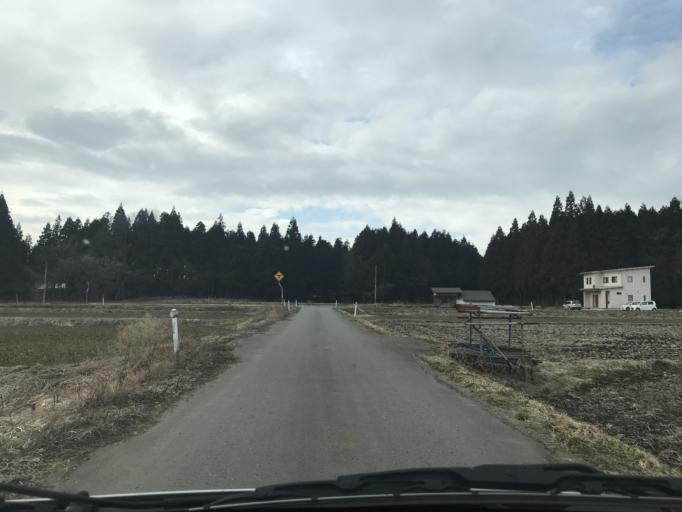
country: JP
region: Iwate
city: Kitakami
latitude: 39.3043
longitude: 141.0014
